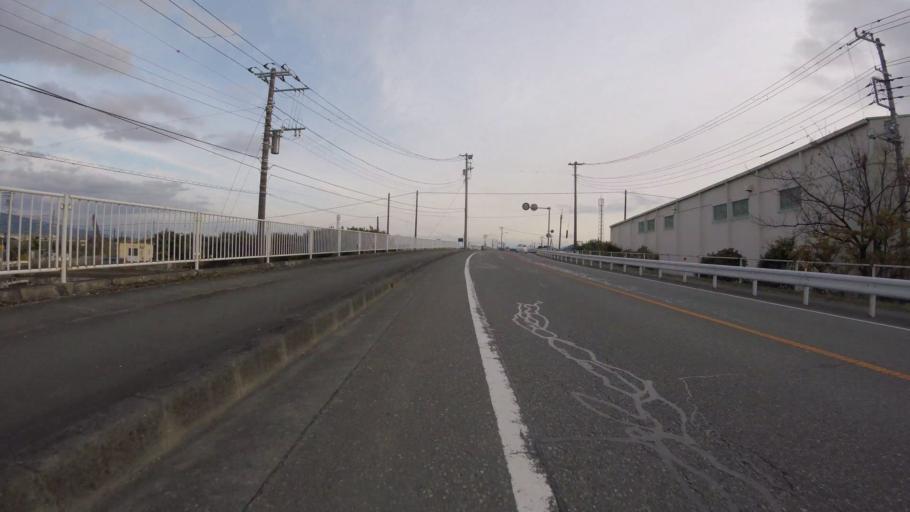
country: JP
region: Shizuoka
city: Fuji
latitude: 35.1459
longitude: 138.7179
